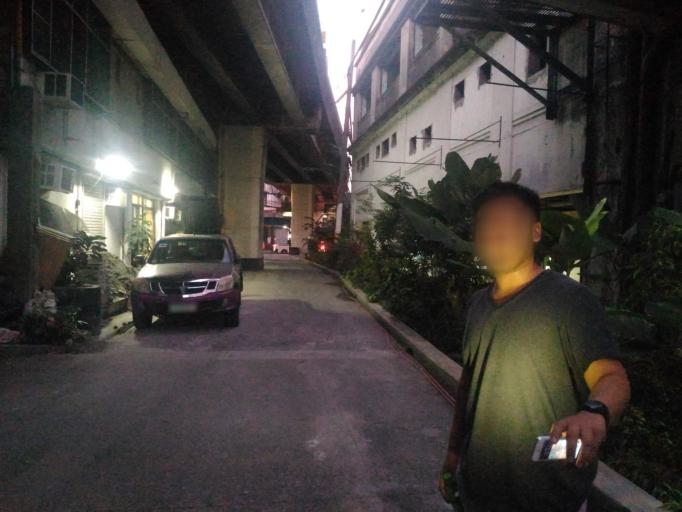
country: PH
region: Metro Manila
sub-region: City of Manila
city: Quiapo
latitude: 14.5977
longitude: 120.9810
